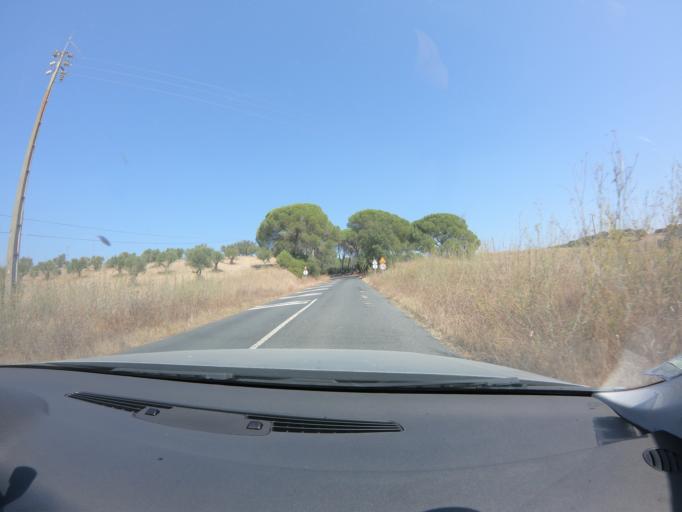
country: PT
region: Setubal
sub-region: Alcacer do Sal
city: Alcacer do Sal
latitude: 38.2880
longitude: -8.4048
